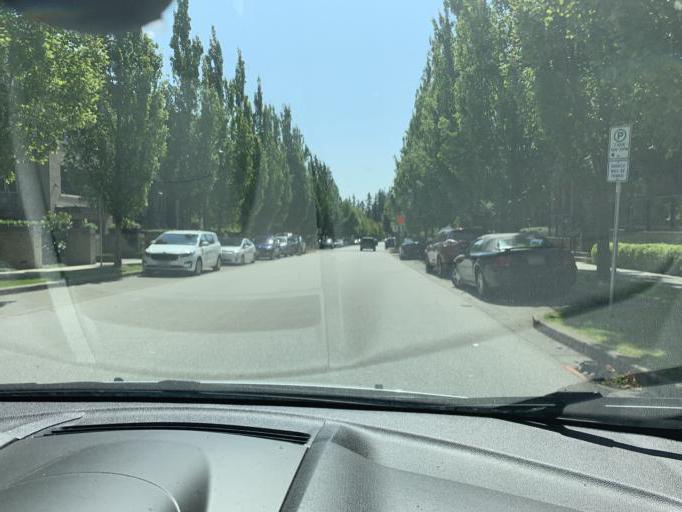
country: CA
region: British Columbia
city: West End
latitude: 49.2537
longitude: -123.2346
